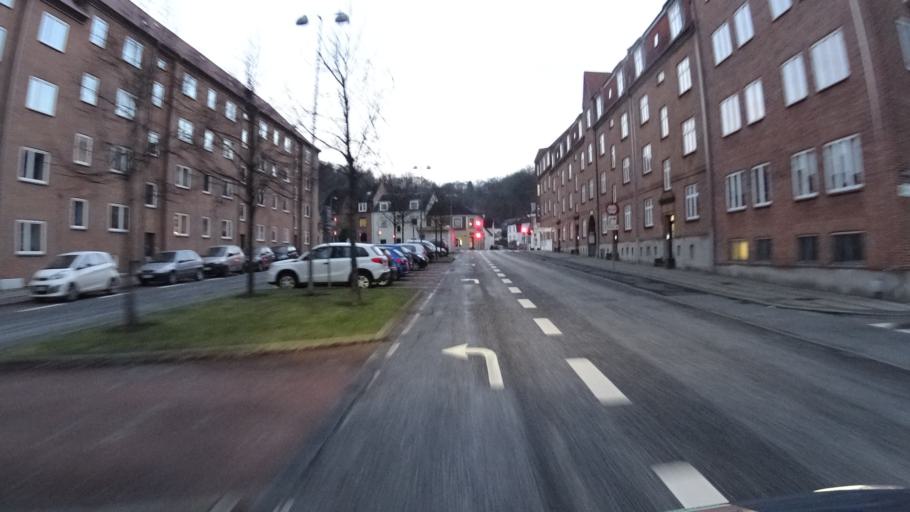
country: DK
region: South Denmark
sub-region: Vejle Kommune
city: Vejle
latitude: 55.7150
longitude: 9.5229
